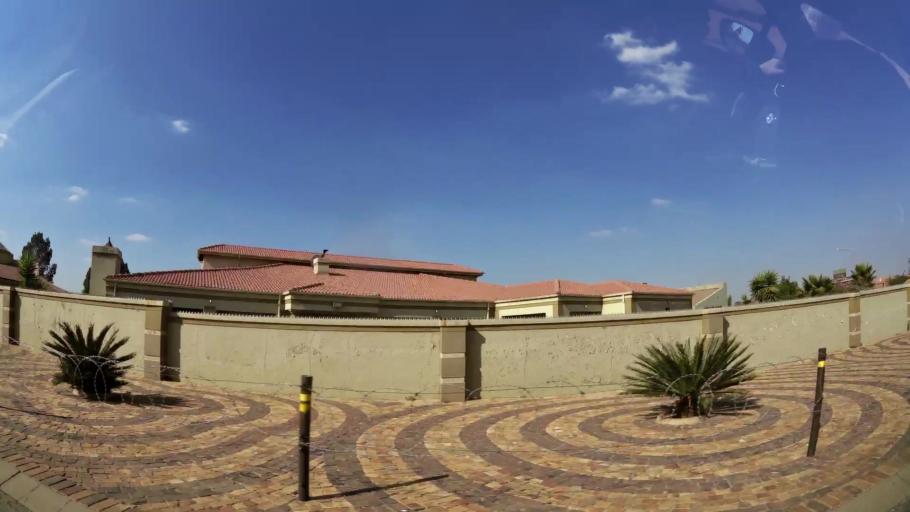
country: ZA
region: Gauteng
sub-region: City of Johannesburg Metropolitan Municipality
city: Roodepoort
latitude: -26.1688
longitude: 27.8034
